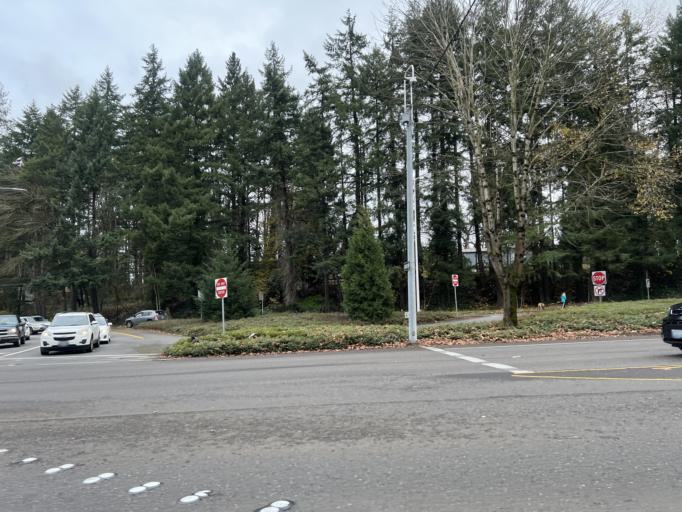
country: US
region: Oregon
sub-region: Marion County
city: Salem
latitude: 44.8942
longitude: -123.0364
